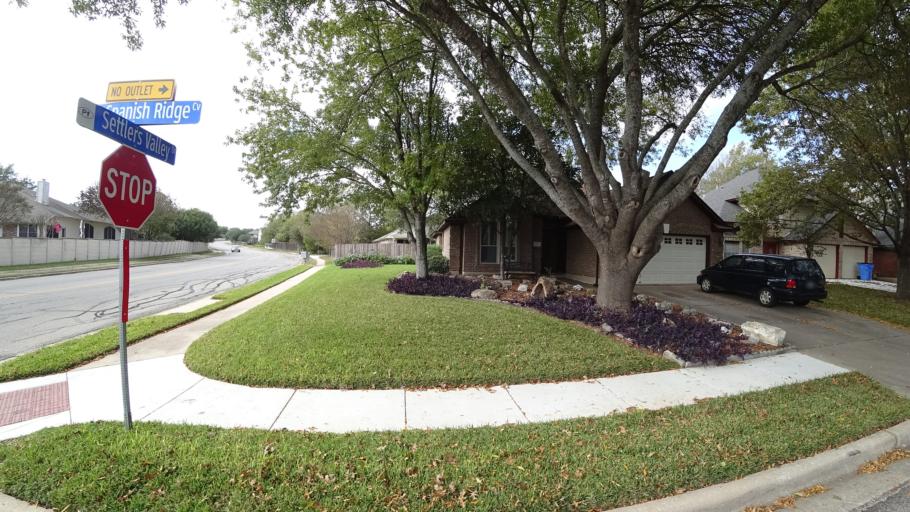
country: US
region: Texas
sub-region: Travis County
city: Pflugerville
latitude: 30.4411
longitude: -97.6355
